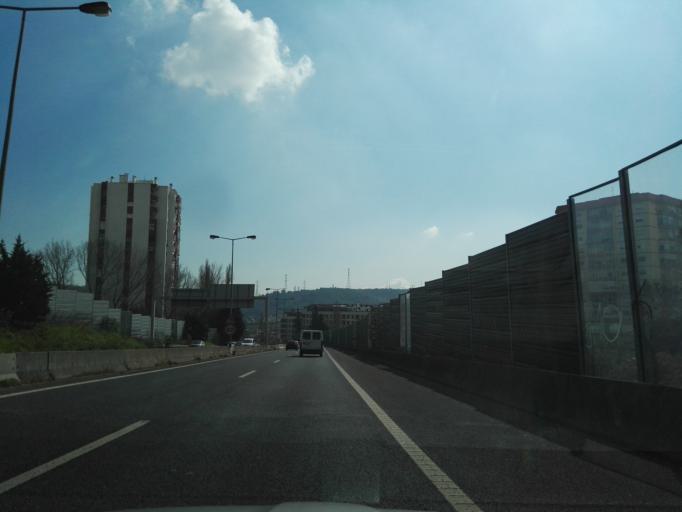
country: PT
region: Lisbon
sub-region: Odivelas
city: Povoa de Santo Adriao
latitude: 38.7957
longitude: -9.1739
